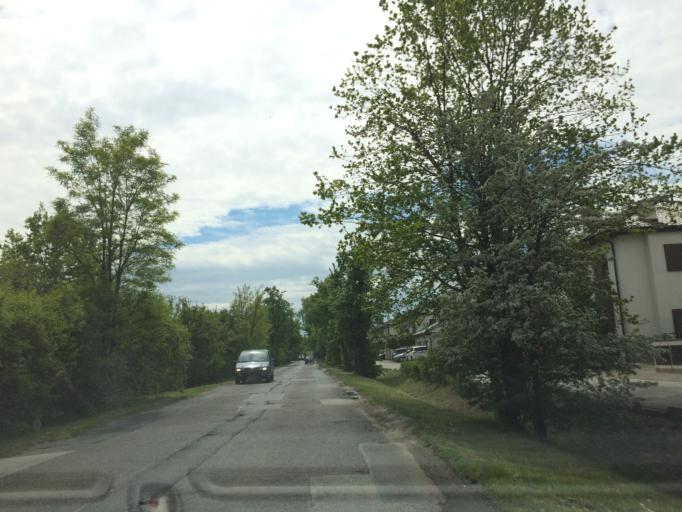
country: PL
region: Lower Silesian Voivodeship
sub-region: Powiat wroclawski
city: Smolec
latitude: 51.1619
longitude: 16.8780
